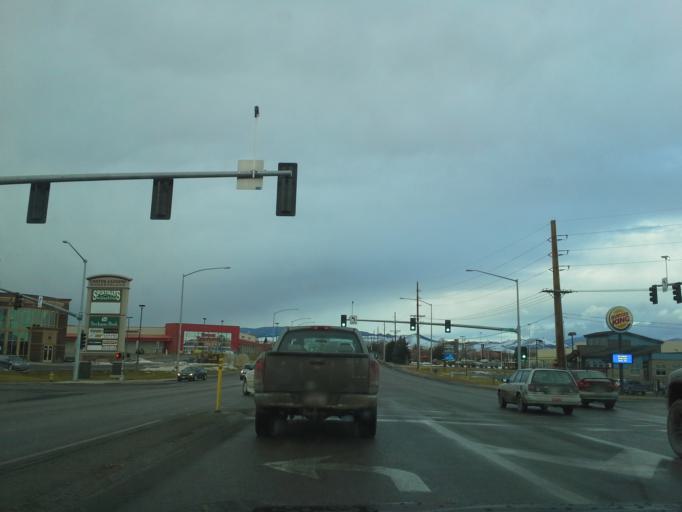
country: US
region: Montana
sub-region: Lewis and Clark County
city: Helena
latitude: 46.6166
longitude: -112.0150
